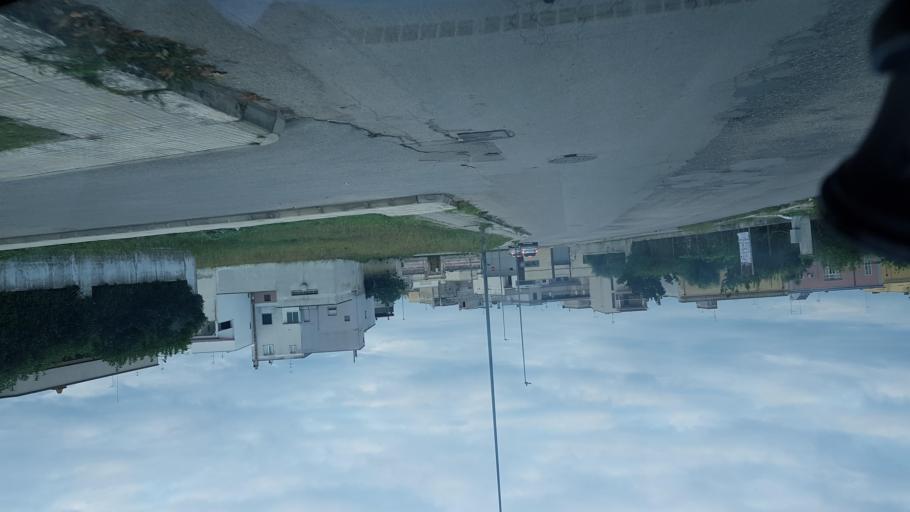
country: IT
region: Apulia
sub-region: Provincia di Brindisi
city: Oria
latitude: 40.5046
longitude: 17.6463
